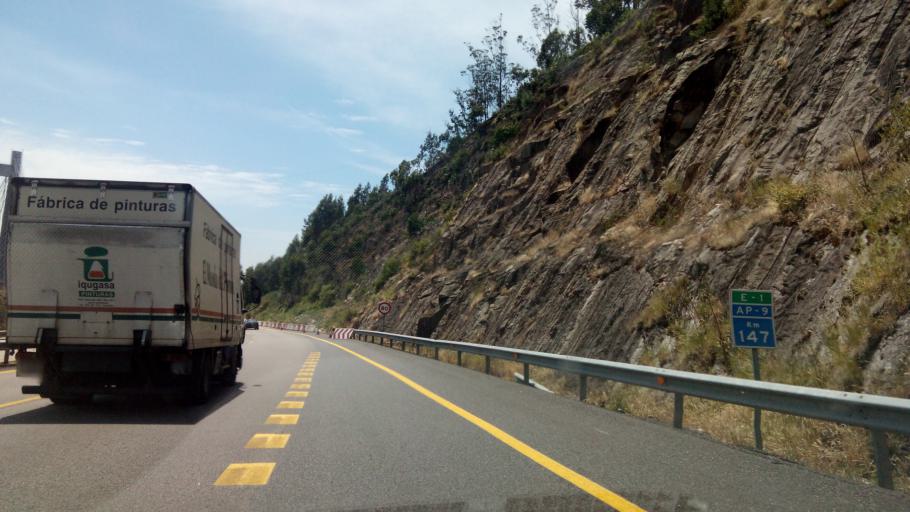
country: ES
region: Galicia
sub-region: Provincia de Pontevedra
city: Redondela
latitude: 42.2945
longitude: -8.6587
